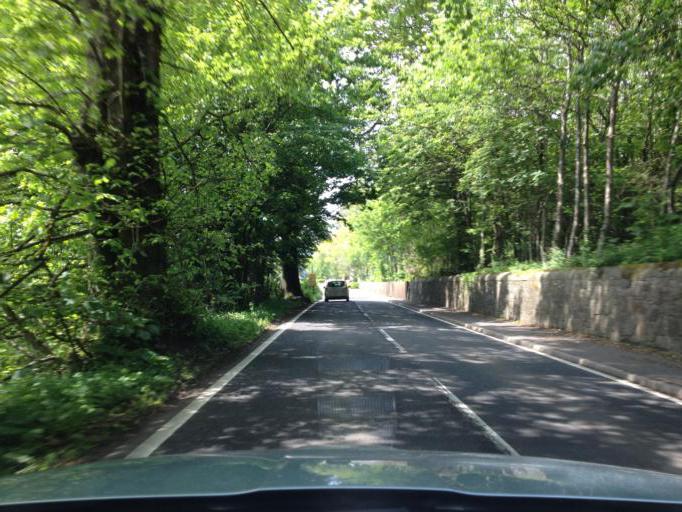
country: GB
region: Scotland
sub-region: Renfrewshire
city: Bishopton
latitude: 55.9149
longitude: -4.4828
